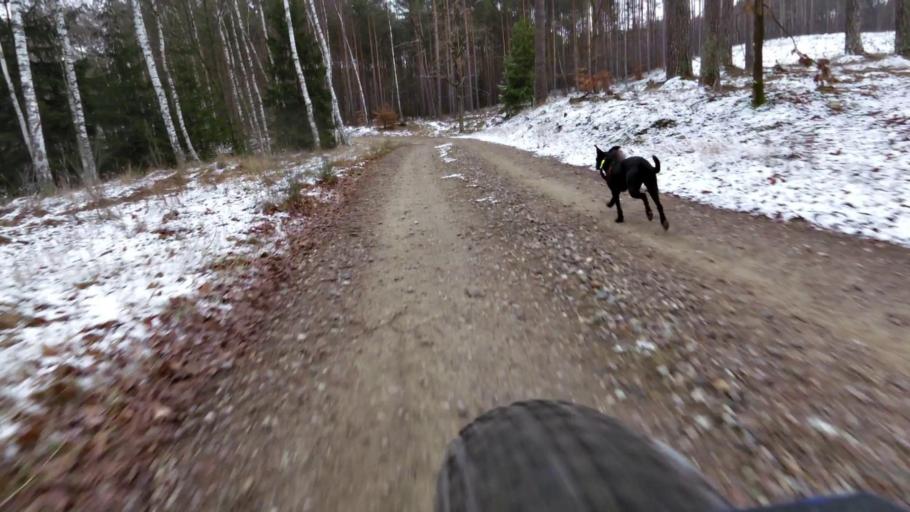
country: PL
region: West Pomeranian Voivodeship
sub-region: Powiat walecki
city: Miroslawiec
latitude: 53.3230
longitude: 16.0958
